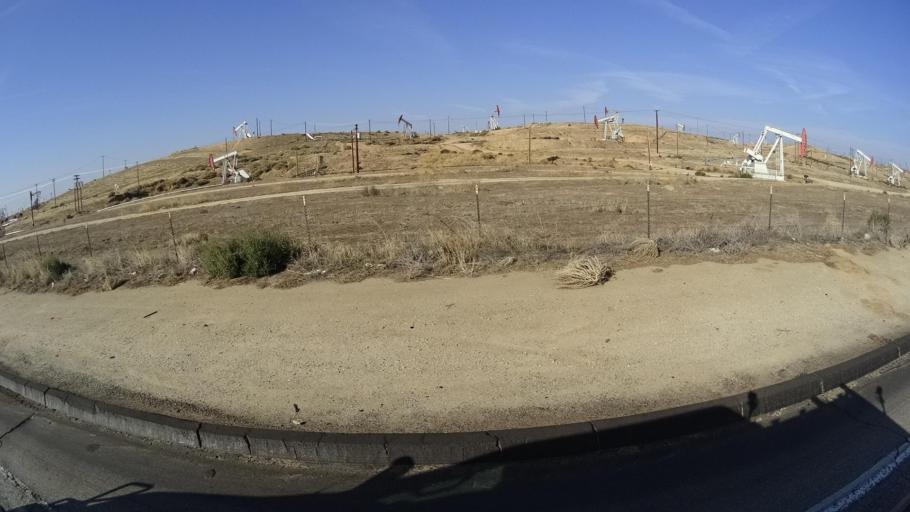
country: US
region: California
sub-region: Kern County
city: Oildale
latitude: 35.4647
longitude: -119.0255
